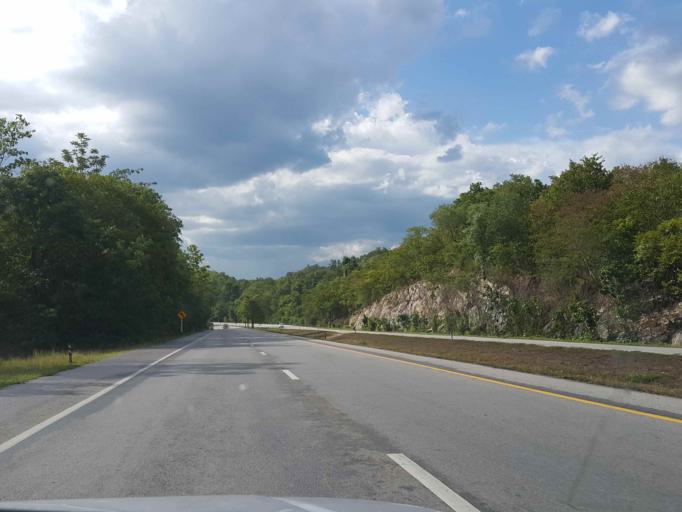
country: TH
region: Lampang
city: Thoen
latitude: 17.6831
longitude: 99.2402
